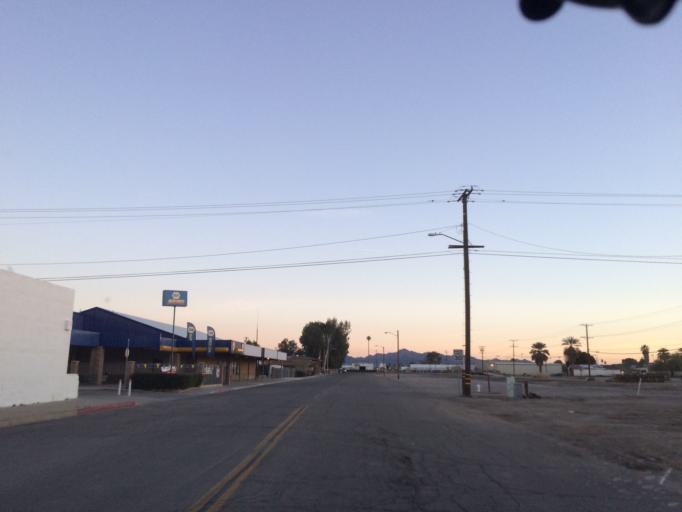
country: US
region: California
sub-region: Riverside County
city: Blythe
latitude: 33.6105
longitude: -114.6008
